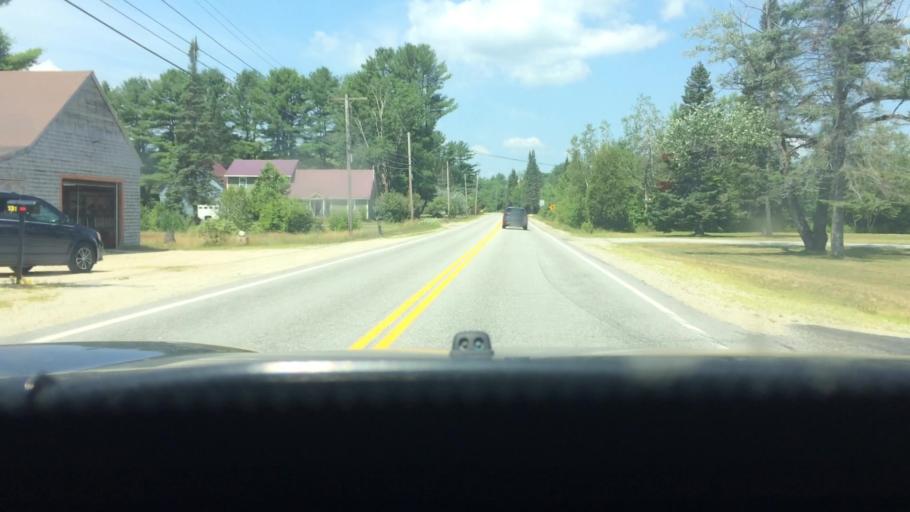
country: US
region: Maine
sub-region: Oxford County
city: Oxford
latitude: 44.1333
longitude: -70.4509
